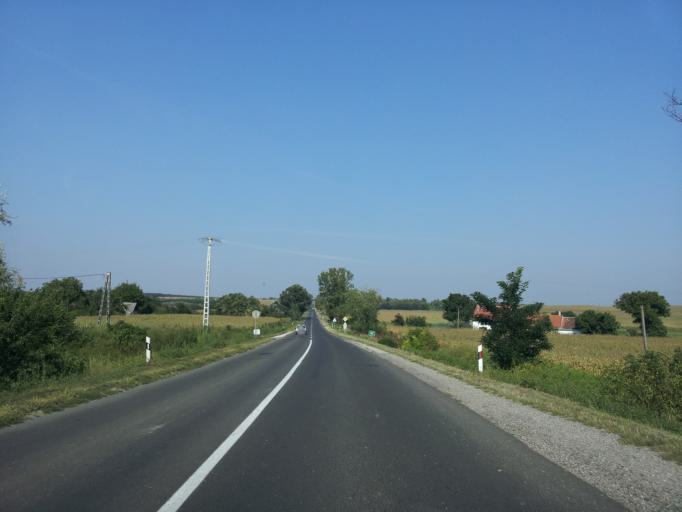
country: HU
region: Fejer
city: Lepseny
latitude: 47.0070
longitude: 18.2634
